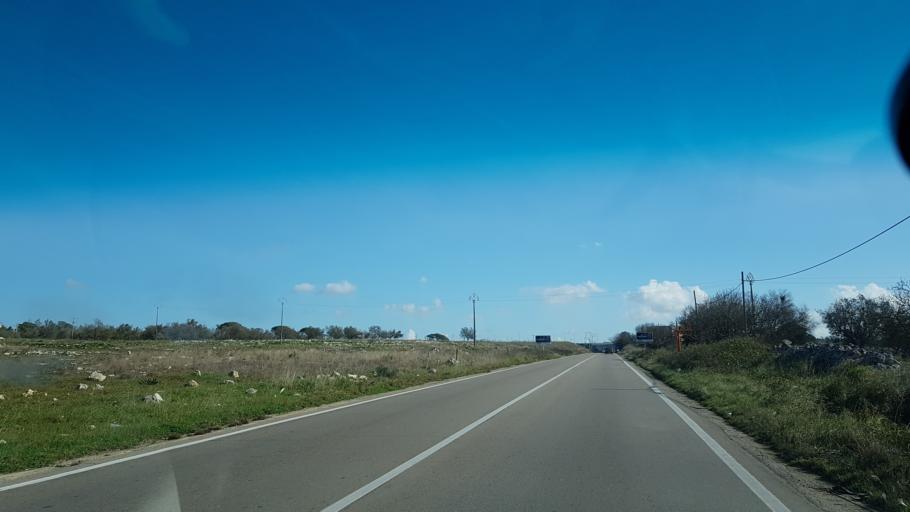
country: IT
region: Apulia
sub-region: Provincia di Lecce
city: Giorgilorio
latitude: 40.3568
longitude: 18.1281
